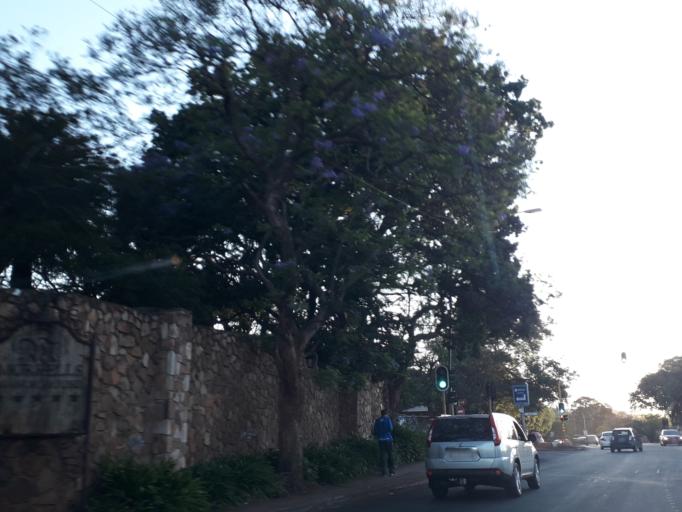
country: ZA
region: Gauteng
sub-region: City of Johannesburg Metropolitan Municipality
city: Roodepoort
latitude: -26.1366
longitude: 27.9614
